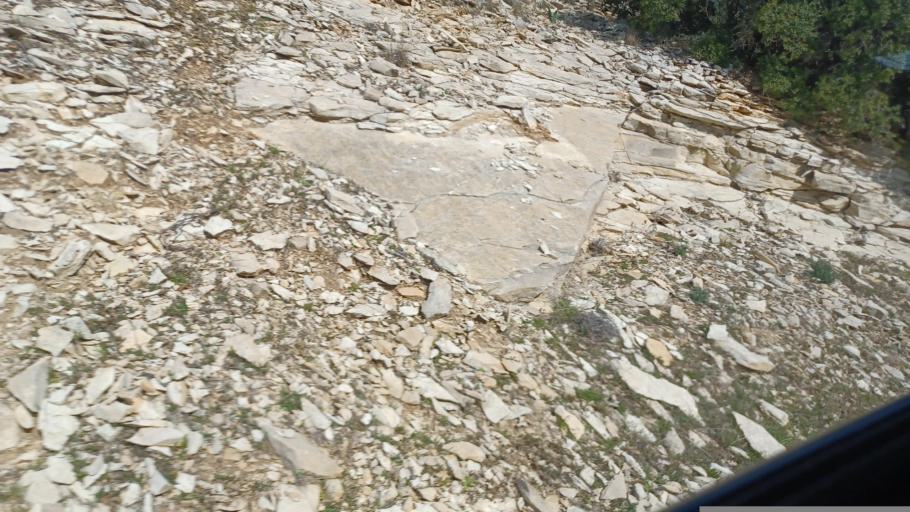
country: CY
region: Limassol
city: Pano Polemidia
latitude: 34.7956
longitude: 32.9907
